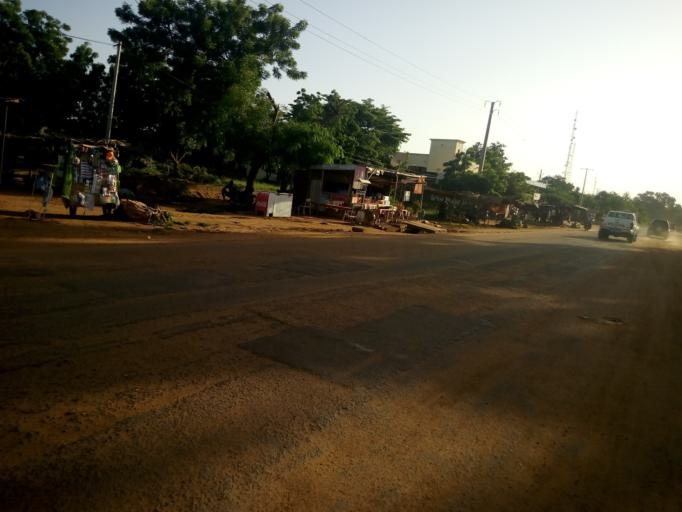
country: ML
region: Segou
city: Segou
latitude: 13.4450
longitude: -6.2649
